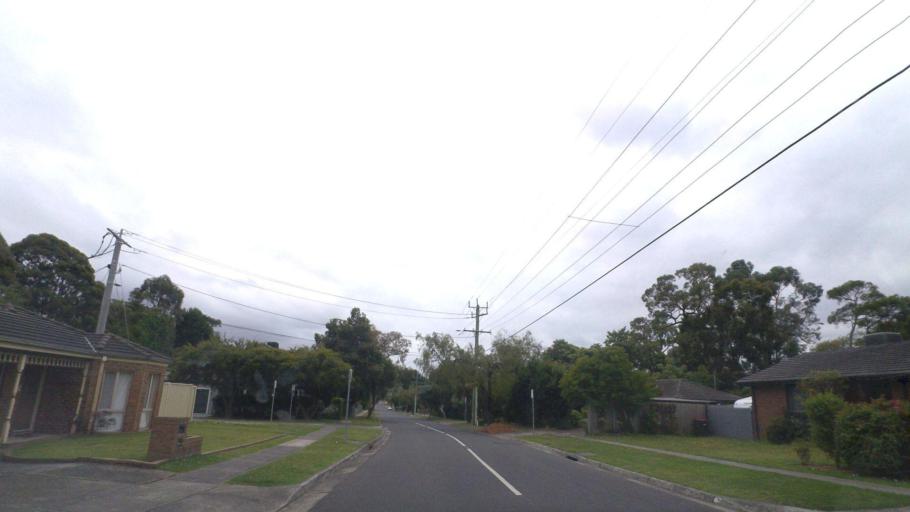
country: AU
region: Victoria
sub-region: Knox
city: The Basin
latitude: -37.8546
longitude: 145.3033
